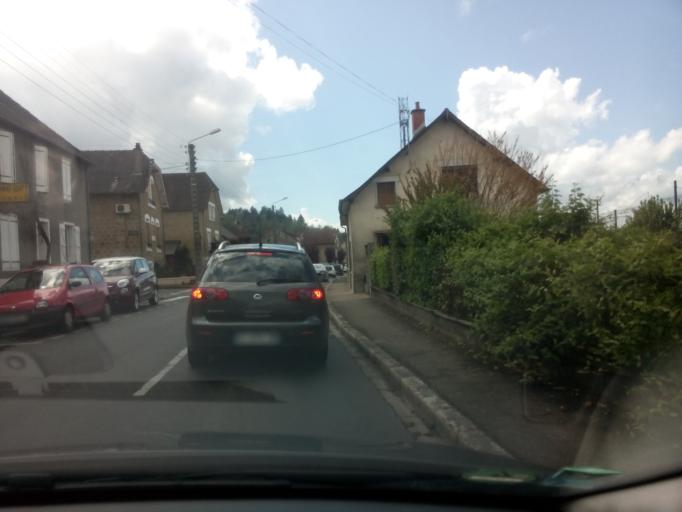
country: FR
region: Limousin
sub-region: Departement de la Correze
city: Brive-la-Gaillarde
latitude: 45.1489
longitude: 1.5114
